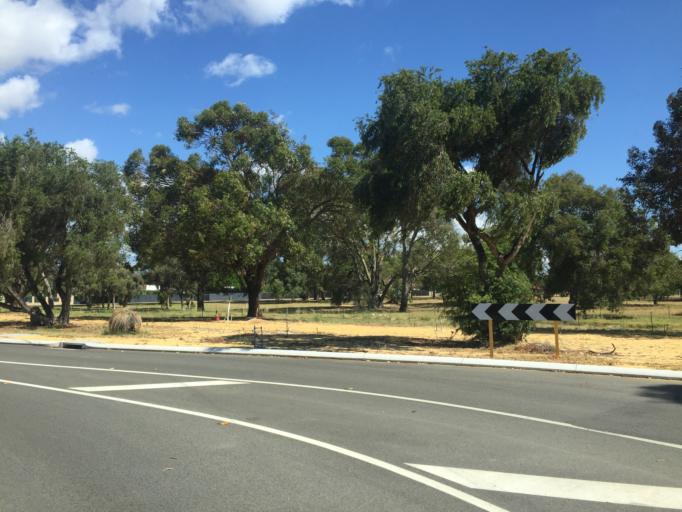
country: AU
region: Western Australia
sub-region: Belmont
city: Redcliffe
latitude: -31.9323
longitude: 115.9442
